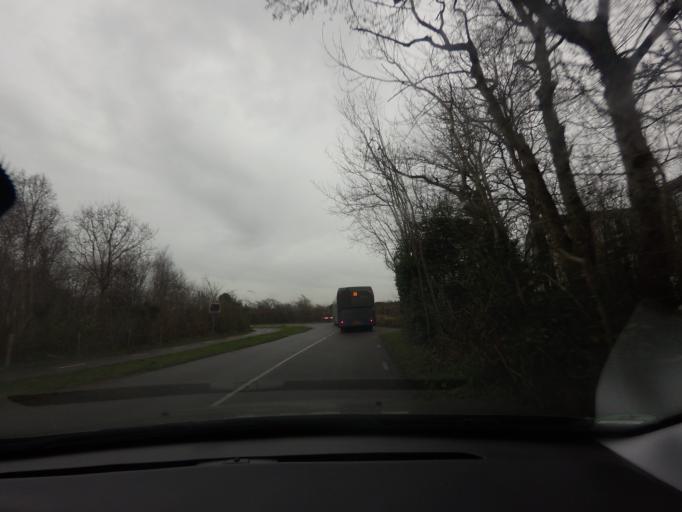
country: NL
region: North Holland
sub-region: Gemeente Texel
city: Den Burg
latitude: 53.0765
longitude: 4.7555
